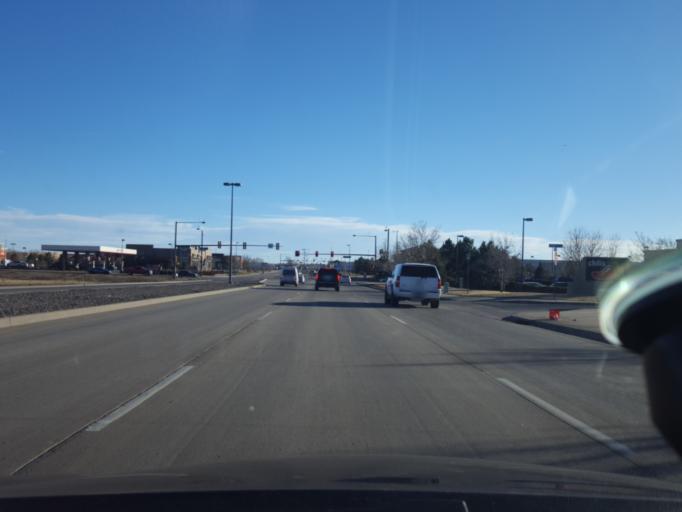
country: US
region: Colorado
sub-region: Adams County
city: Aurora
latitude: 39.7660
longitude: -104.7723
